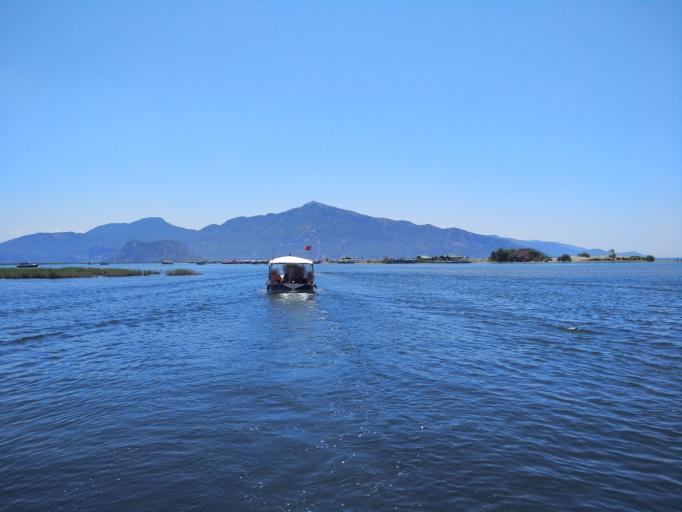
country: TR
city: Dalyan
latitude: 36.8046
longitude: 28.6043
